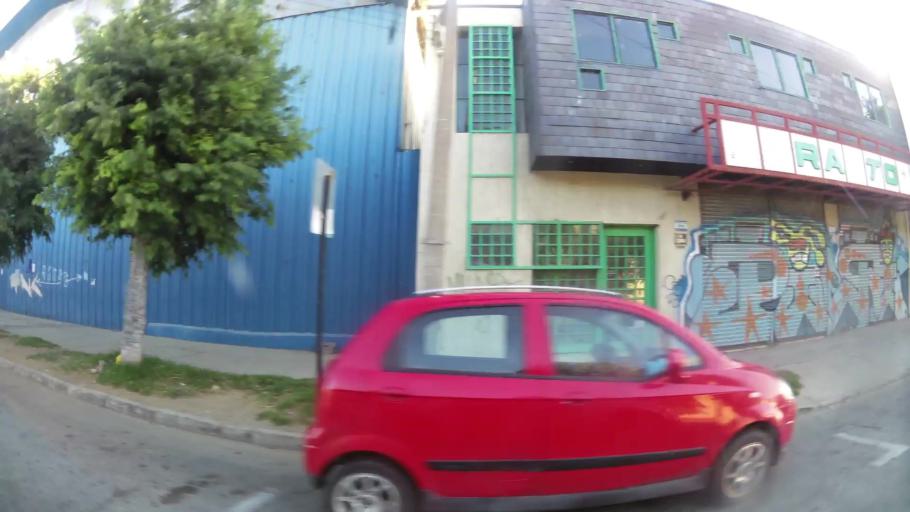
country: CL
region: Valparaiso
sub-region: Provincia de Valparaiso
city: Vina del Mar
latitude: -33.0252
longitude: -71.5441
